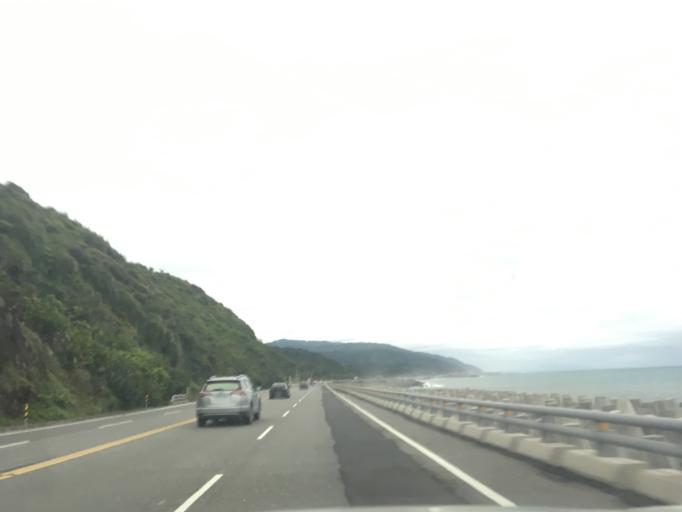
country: TW
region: Taiwan
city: Hengchun
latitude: 22.3193
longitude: 120.8917
